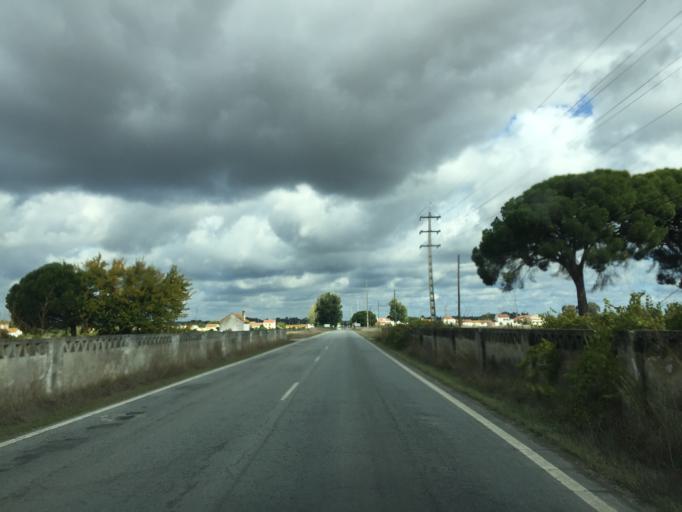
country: PT
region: Santarem
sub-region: Coruche
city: Coruche
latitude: 38.9506
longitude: -8.4965
